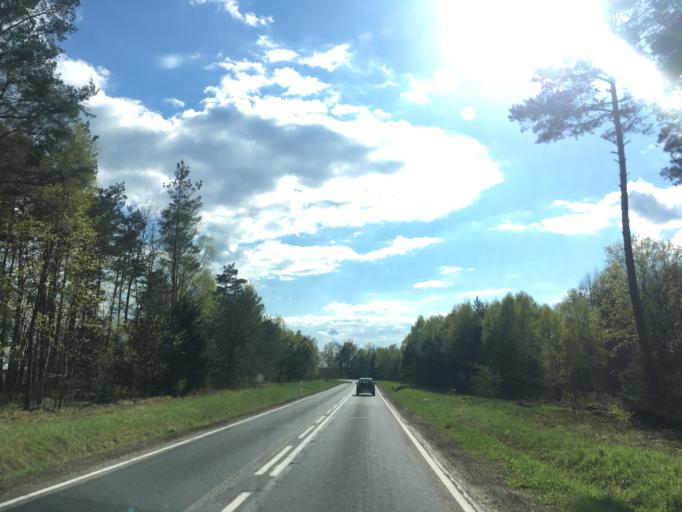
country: PL
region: Warmian-Masurian Voivodeship
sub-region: Powiat szczycienski
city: Pasym
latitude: 53.5522
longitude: 20.8611
